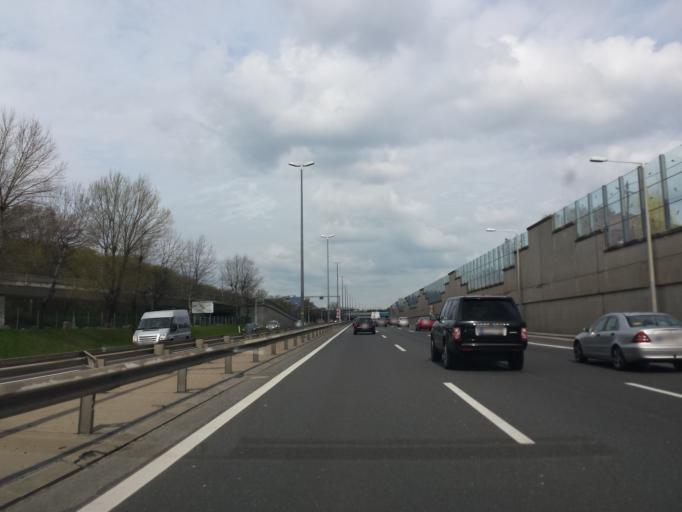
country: AT
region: Vienna
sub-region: Wien Stadt
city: Vienna
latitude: 48.2407
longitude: 16.4014
